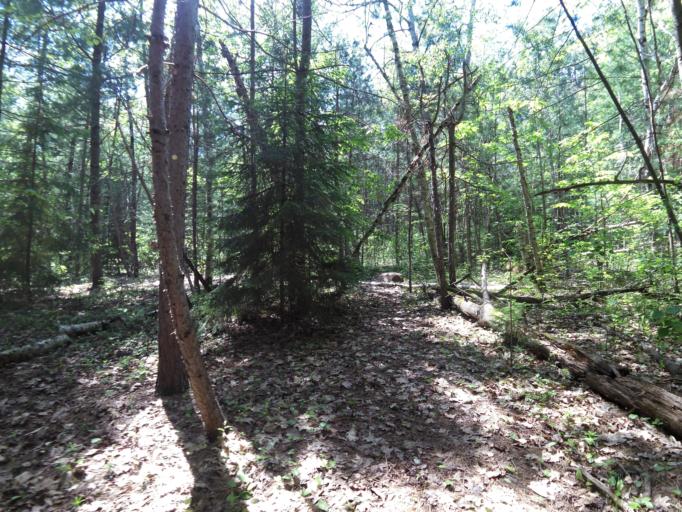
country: CA
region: Ontario
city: Bells Corners
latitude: 45.3202
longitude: -75.7388
